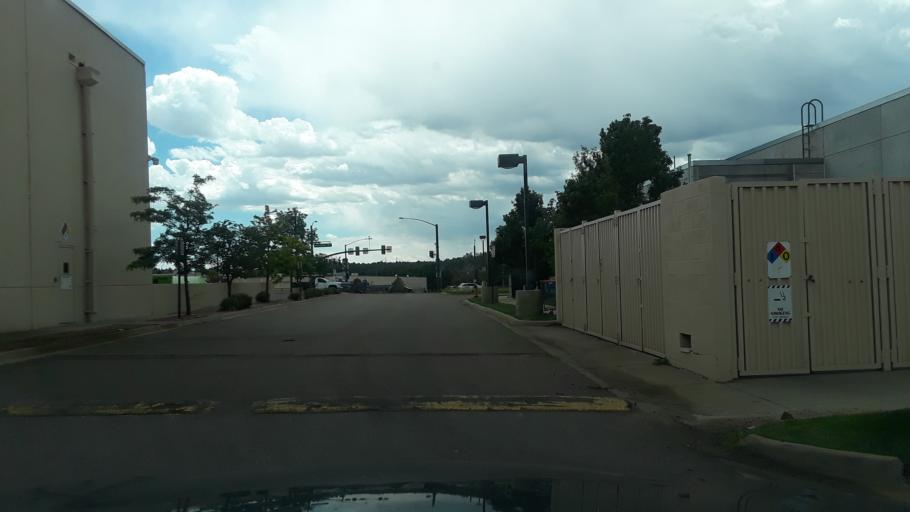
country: US
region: Colorado
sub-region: El Paso County
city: Air Force Academy
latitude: 38.9342
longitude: -104.7993
